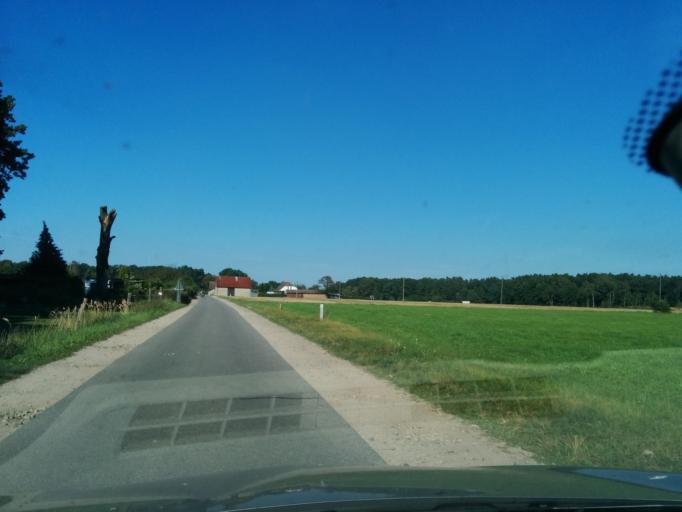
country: DE
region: Mecklenburg-Vorpommern
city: Torgelow
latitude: 53.6429
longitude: 14.0260
